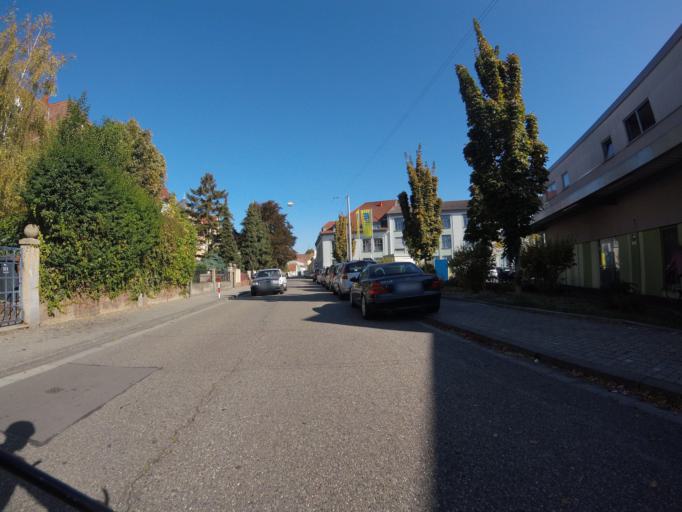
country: DE
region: Rheinland-Pfalz
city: Speyer
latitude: 49.3129
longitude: 8.4381
